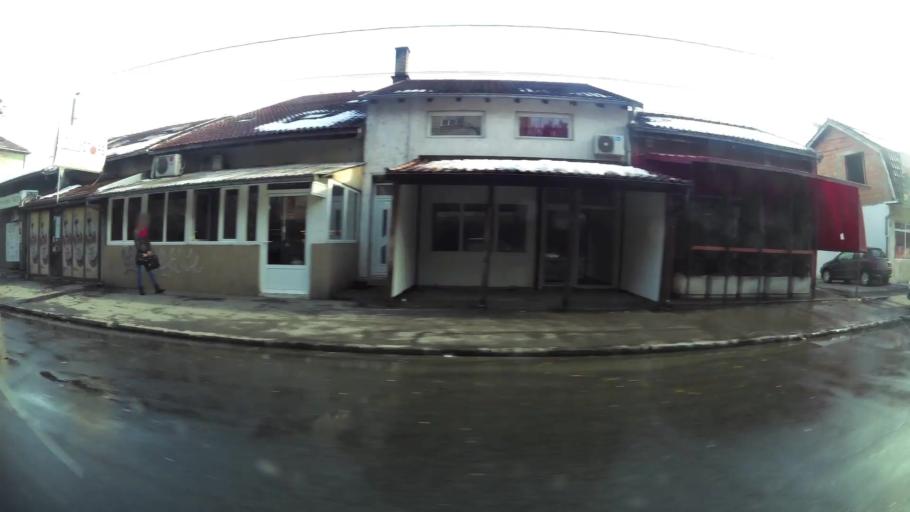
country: RS
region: Central Serbia
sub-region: Belgrade
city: Rakovica
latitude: 44.7414
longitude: 20.4328
